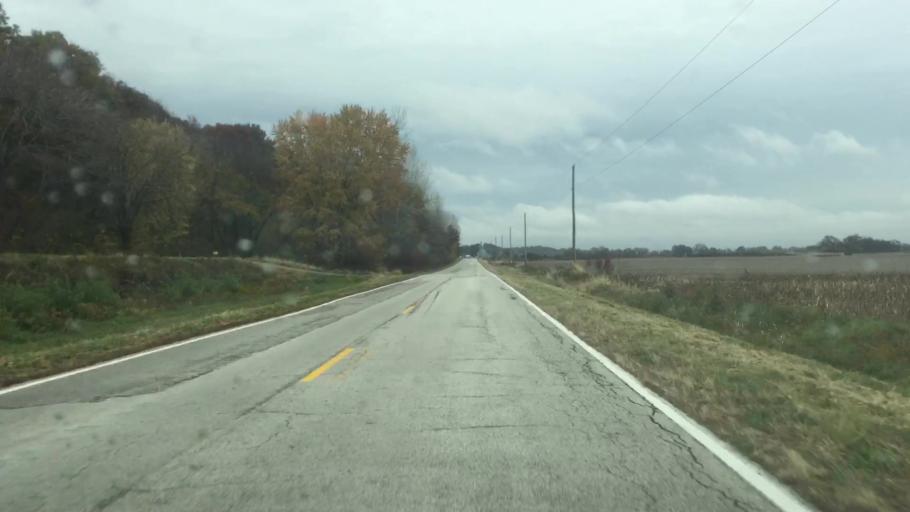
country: US
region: Missouri
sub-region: Gasconade County
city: Hermann
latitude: 38.7098
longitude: -91.5401
